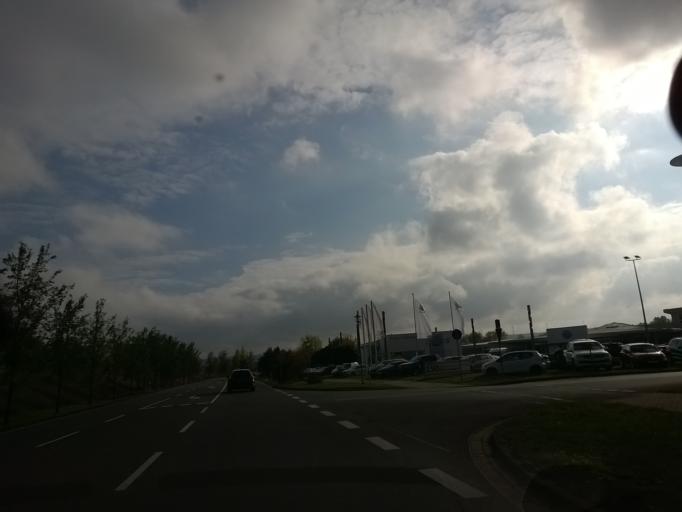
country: DE
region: Thuringia
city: Nordhausen
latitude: 51.4768
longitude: 10.8091
